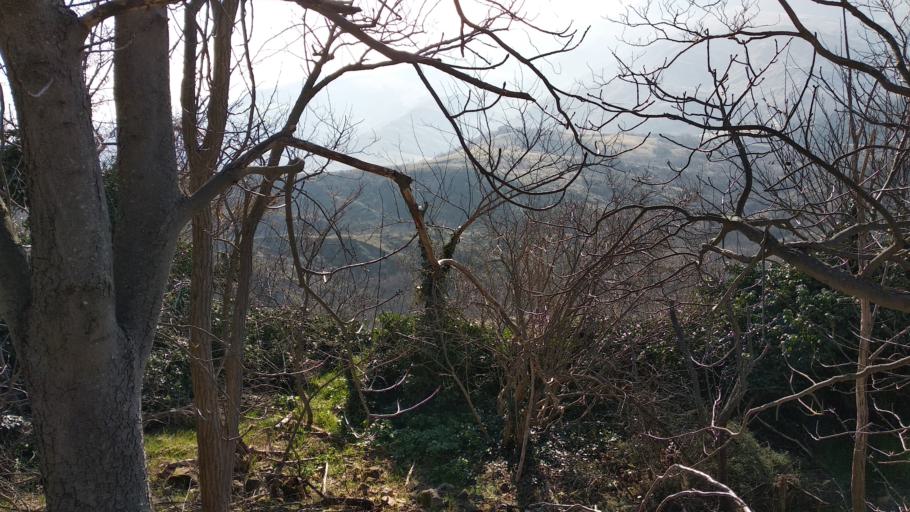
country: IT
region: Emilia-Romagna
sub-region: Provincia di Bologna
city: Ozzano dell'Emilia
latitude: 44.3954
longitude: 11.4627
